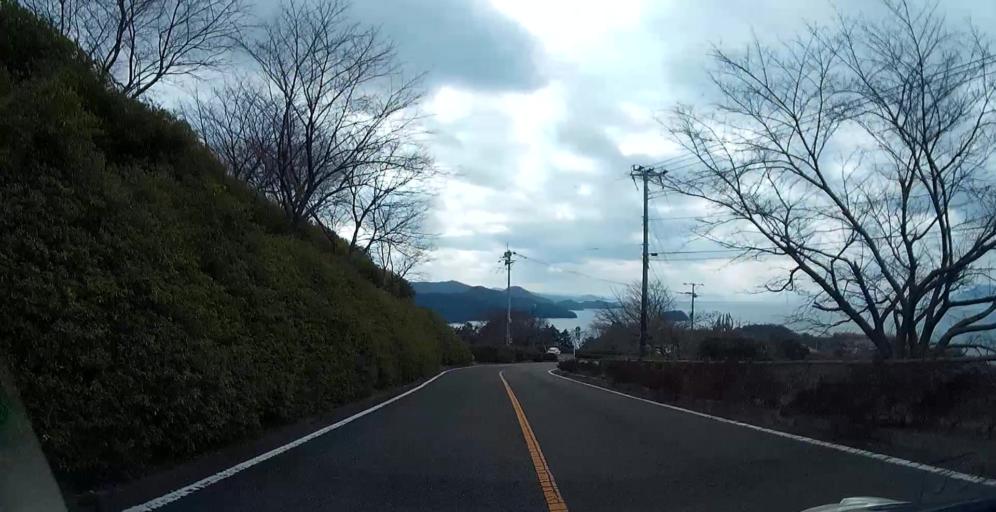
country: JP
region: Kumamoto
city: Yatsushiro
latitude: 32.3693
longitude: 130.4982
